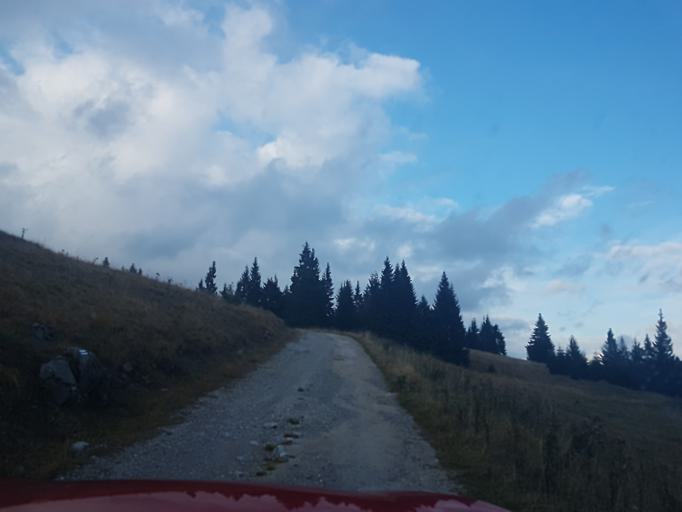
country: SK
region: Zilinsky
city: Ruzomberok
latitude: 48.9889
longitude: 19.2015
